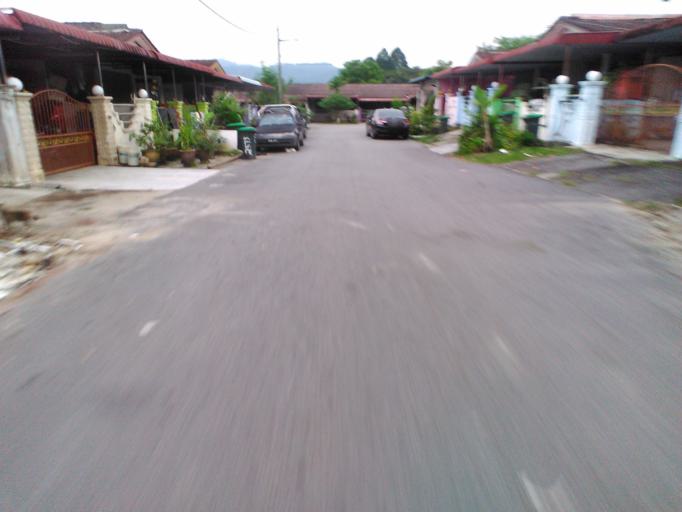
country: MY
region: Kedah
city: Kulim
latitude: 5.3690
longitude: 100.5725
